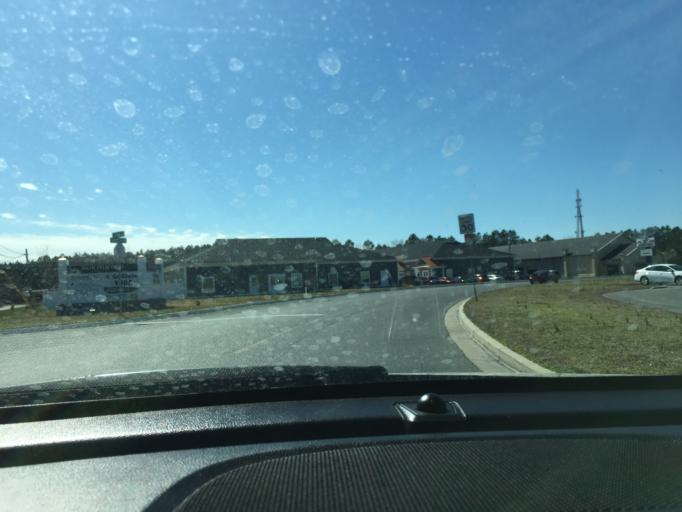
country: US
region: Maryland
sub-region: Wicomico County
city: Salisbury
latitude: 38.4023
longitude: -75.5723
